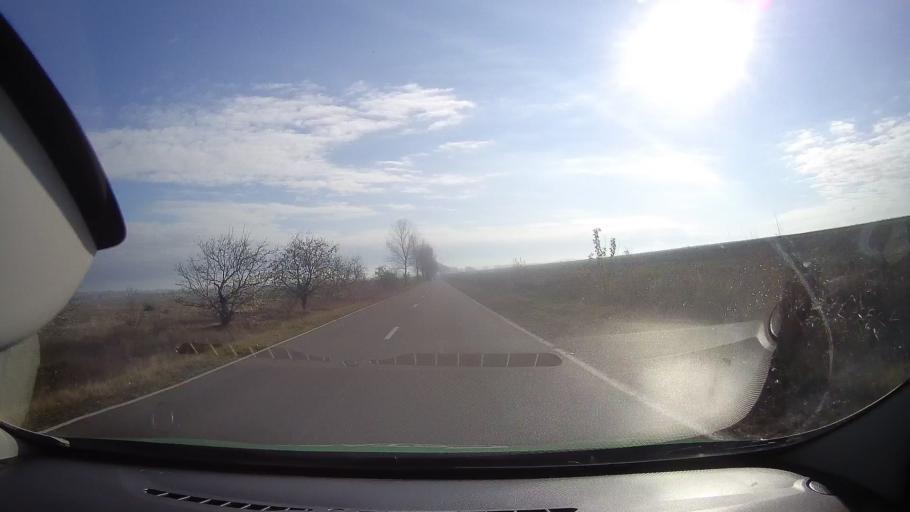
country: RO
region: Tulcea
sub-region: Comuna Mahmudia
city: Mahmudia
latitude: 45.0709
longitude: 29.0964
